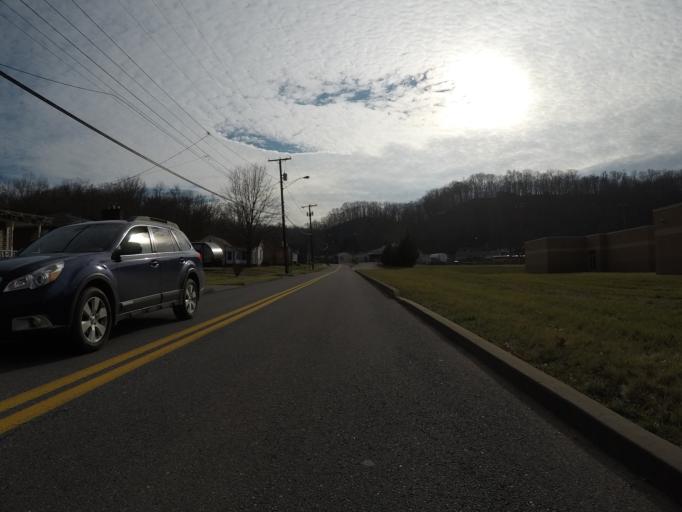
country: US
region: West Virginia
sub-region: Cabell County
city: Barboursville
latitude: 38.4027
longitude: -82.2936
